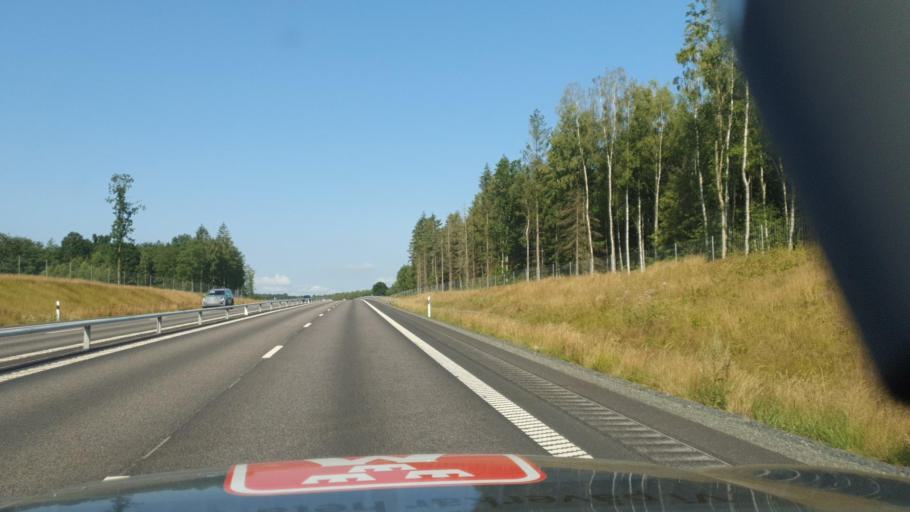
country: SE
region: Skane
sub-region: Hassleholms Kommun
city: Vinslov
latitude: 55.9458
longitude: 13.8835
